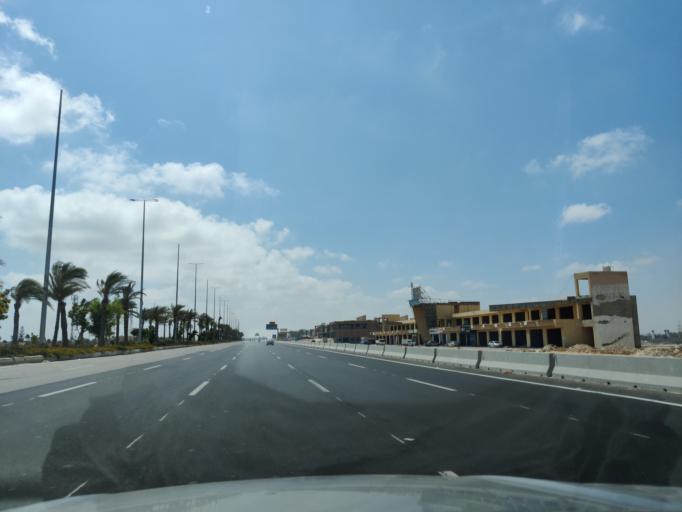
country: EG
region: Muhafazat Matruh
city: Al `Alamayn
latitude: 30.8318
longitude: 28.9666
